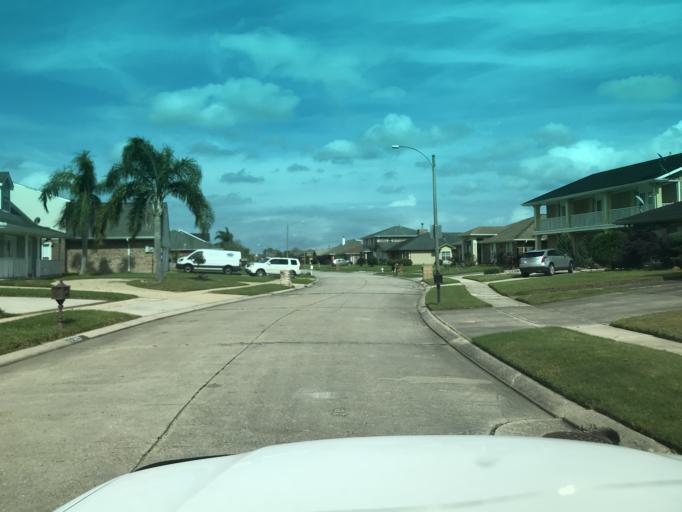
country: US
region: Louisiana
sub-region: Saint Bernard Parish
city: Chalmette
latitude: 30.0326
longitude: -89.9531
